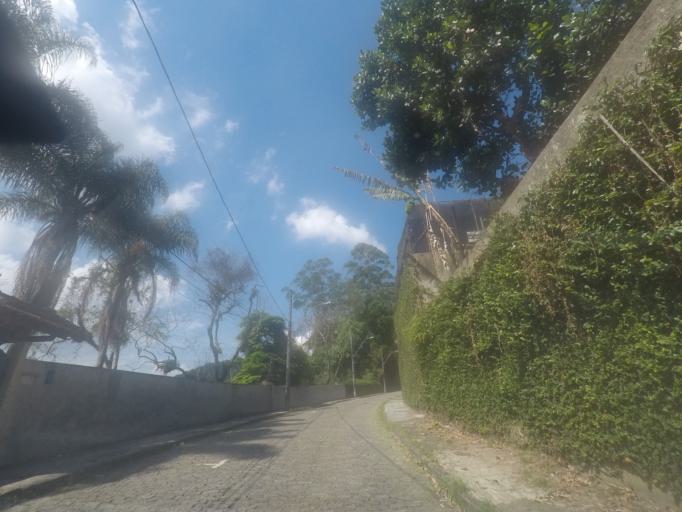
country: BR
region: Rio de Janeiro
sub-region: Petropolis
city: Petropolis
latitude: -22.5090
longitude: -43.1798
